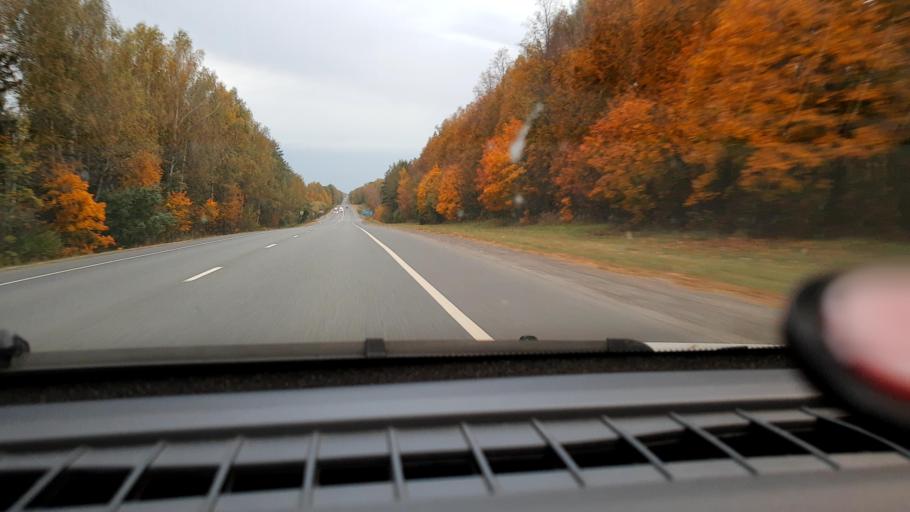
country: RU
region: Vladimir
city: Orgtrud
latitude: 56.2004
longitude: 40.8085
